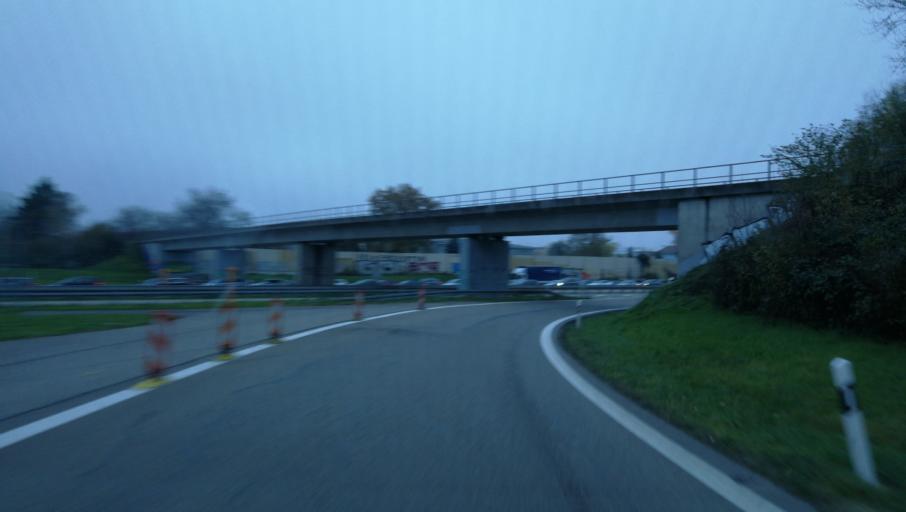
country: DE
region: Baden-Wuerttemberg
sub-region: Freiburg Region
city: Weil am Rhein
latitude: 47.6030
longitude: 7.6023
